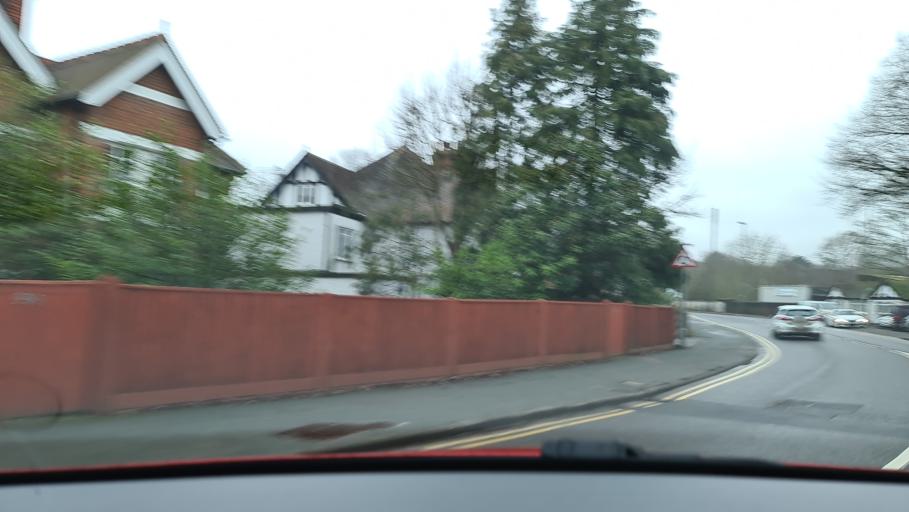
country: GB
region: England
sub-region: Surrey
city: Walton-on-Thames
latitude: 51.3720
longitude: -0.4235
